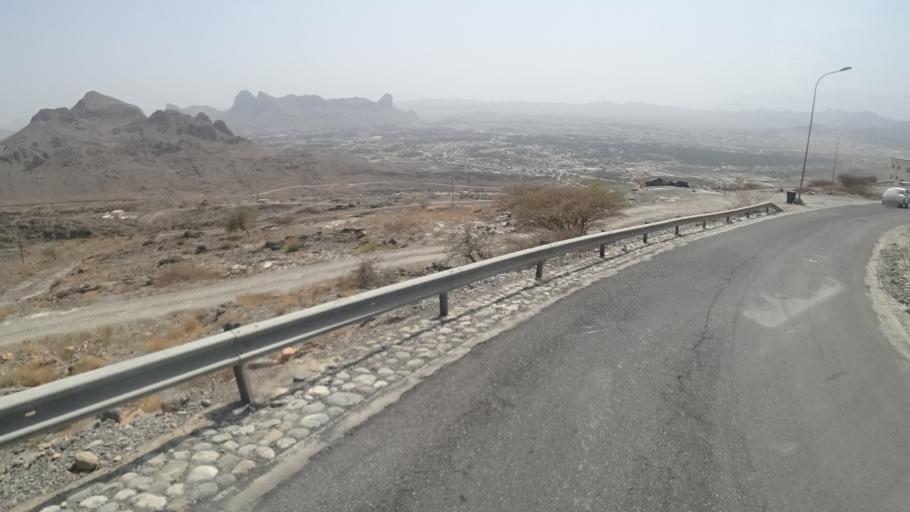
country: OM
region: Muhafazat ad Dakhiliyah
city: Bahla'
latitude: 23.1335
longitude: 57.3056
